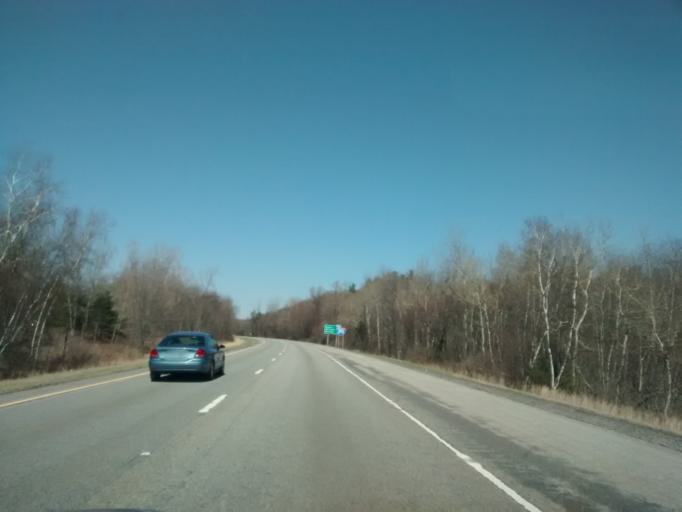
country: US
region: Massachusetts
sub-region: Worcester County
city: Auburn
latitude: 42.1619
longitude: -71.8471
